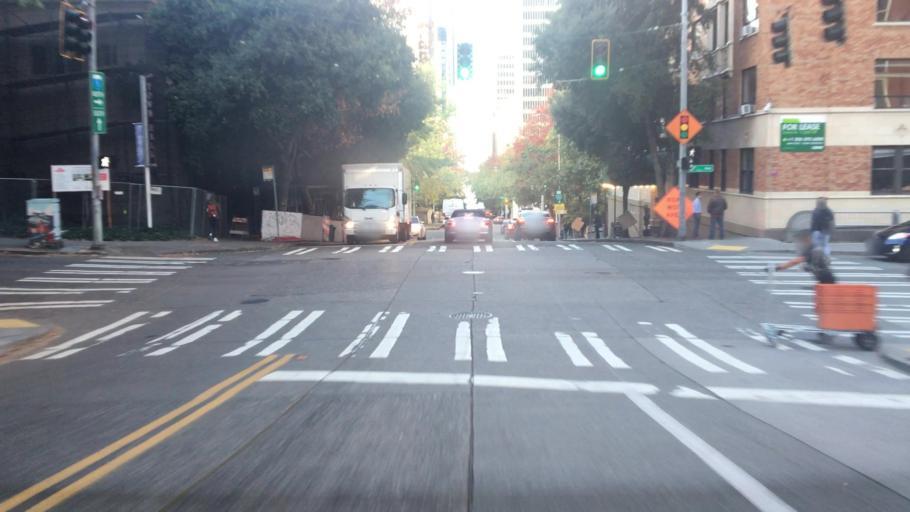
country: US
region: Washington
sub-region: King County
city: Seattle
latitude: 47.6094
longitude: -122.3296
